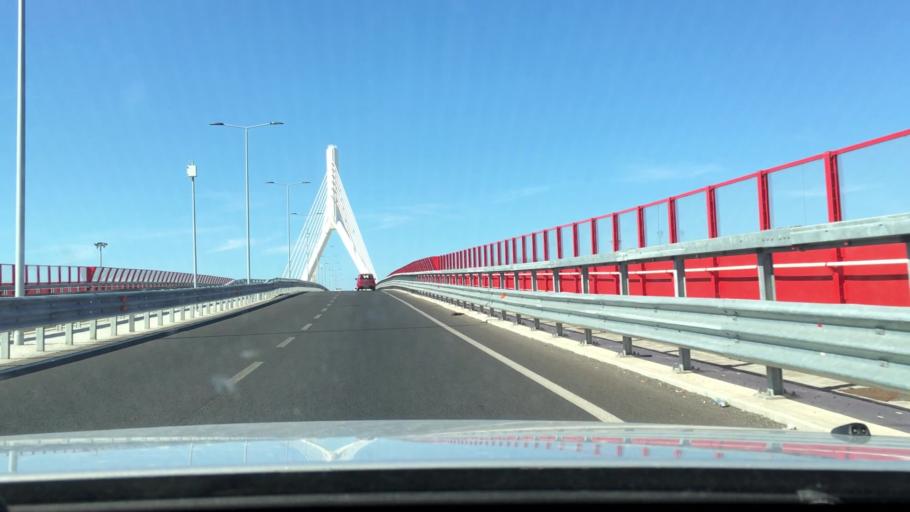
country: IT
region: Apulia
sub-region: Provincia di Bari
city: Bari
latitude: 41.1160
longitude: 16.8486
